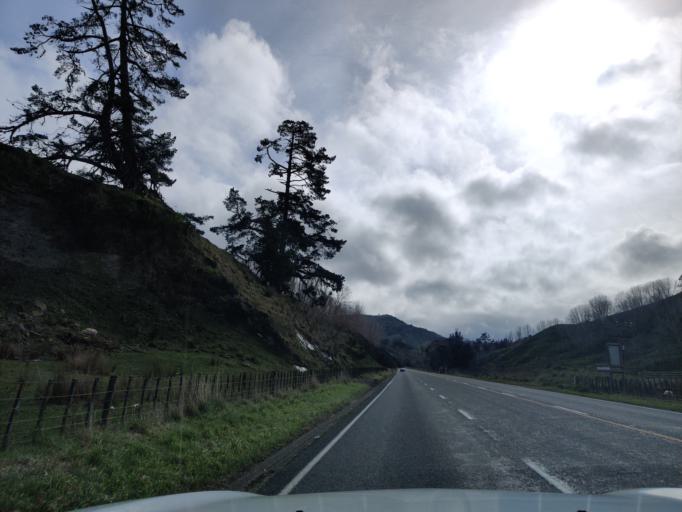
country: NZ
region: Manawatu-Wanganui
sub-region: Ruapehu District
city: Waiouru
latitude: -39.7875
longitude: 175.7854
